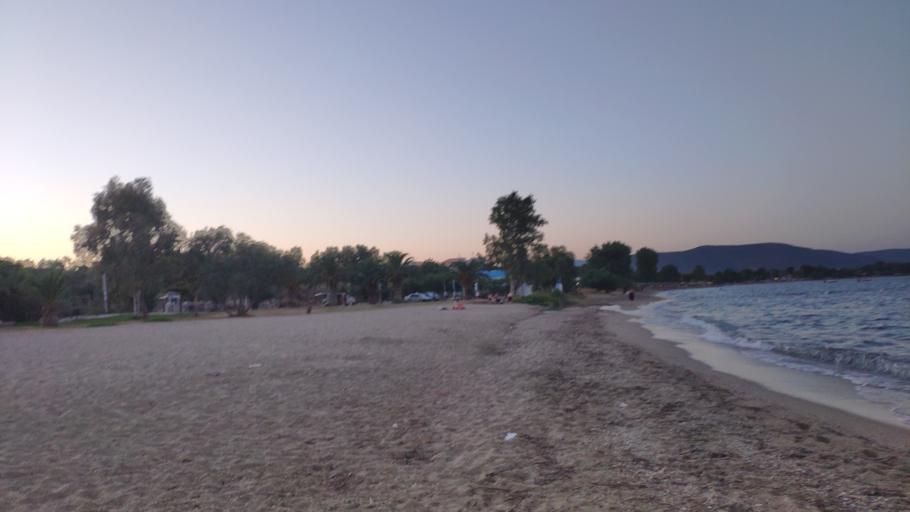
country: GR
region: Attica
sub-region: Nomarchia Anatolikis Attikis
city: Aghios Panteleimon
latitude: 38.1018
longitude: 23.9806
